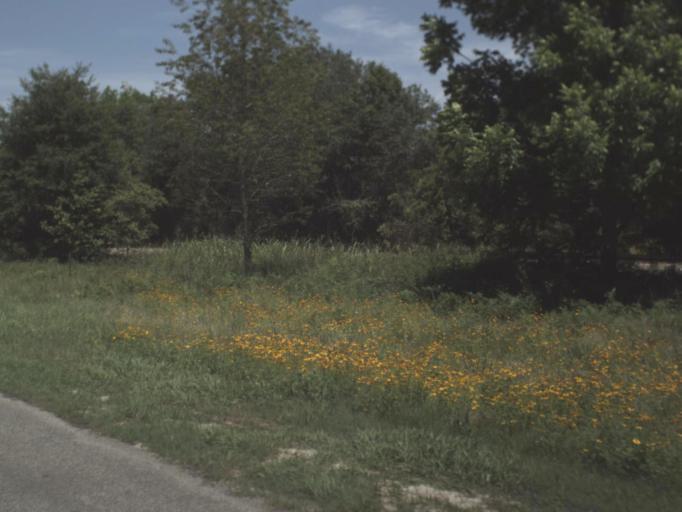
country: US
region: Florida
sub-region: Suwannee County
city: Live Oak
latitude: 30.3357
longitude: -83.0728
